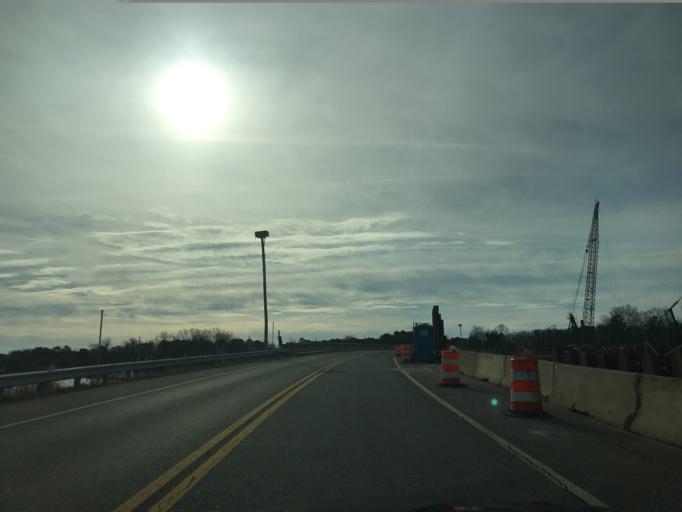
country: US
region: Maryland
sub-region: Charles County
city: Cobb Island
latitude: 38.2672
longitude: -76.8503
